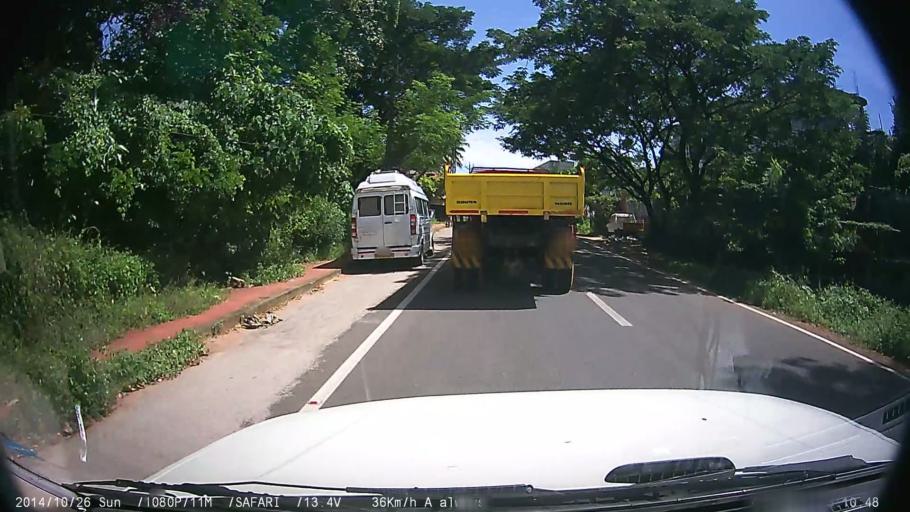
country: IN
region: Kerala
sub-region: Kottayam
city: Changanacheri
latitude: 9.4533
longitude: 76.5438
